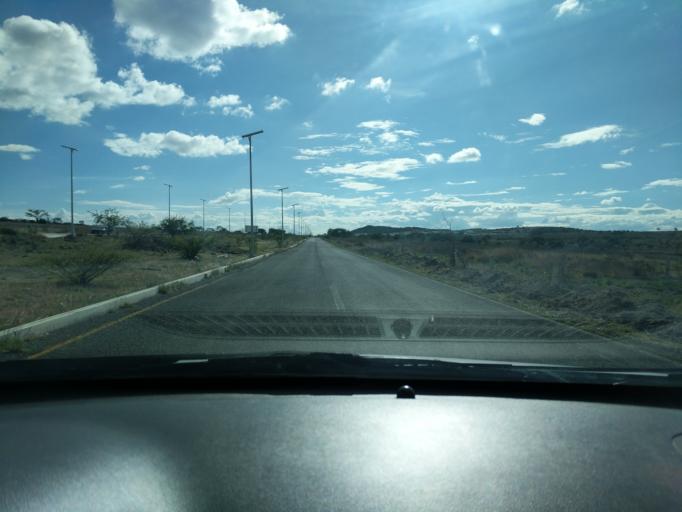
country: MX
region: Queretaro
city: La Canada
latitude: 20.5969
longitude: -100.2960
